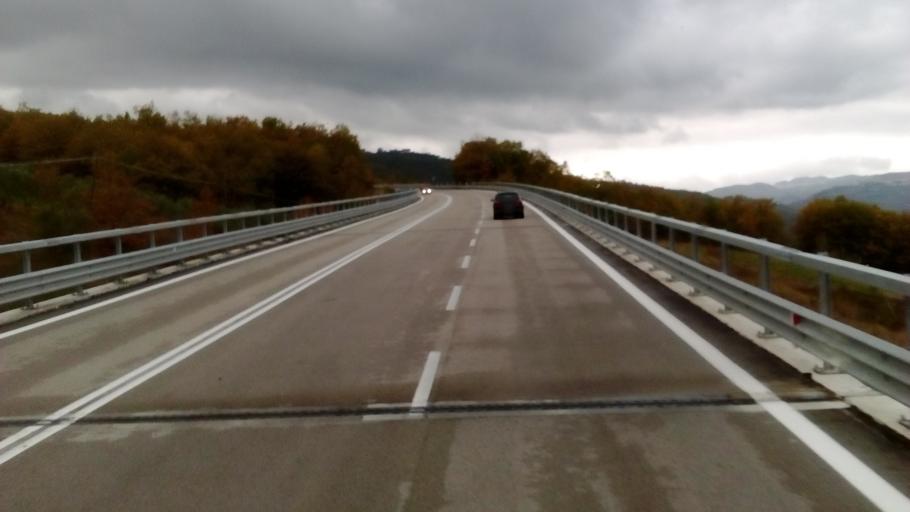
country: IT
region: Molise
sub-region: Provincia di Isernia
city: Bagnoli del Trigno
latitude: 41.7286
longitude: 14.4403
